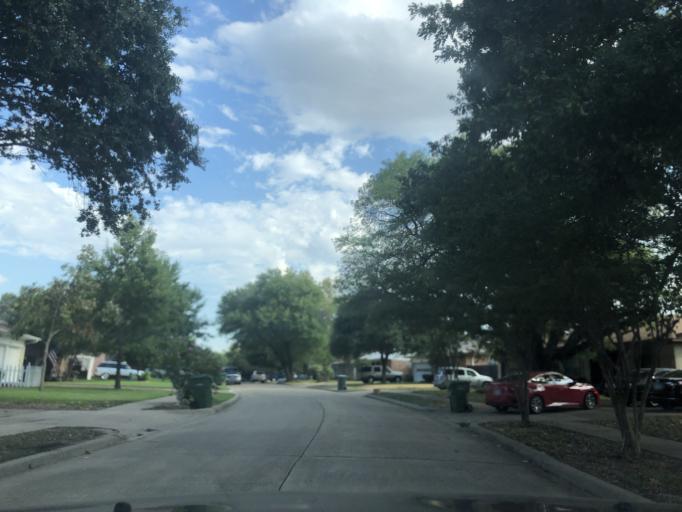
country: US
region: Texas
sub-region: Dallas County
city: Garland
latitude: 32.8887
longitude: -96.6591
